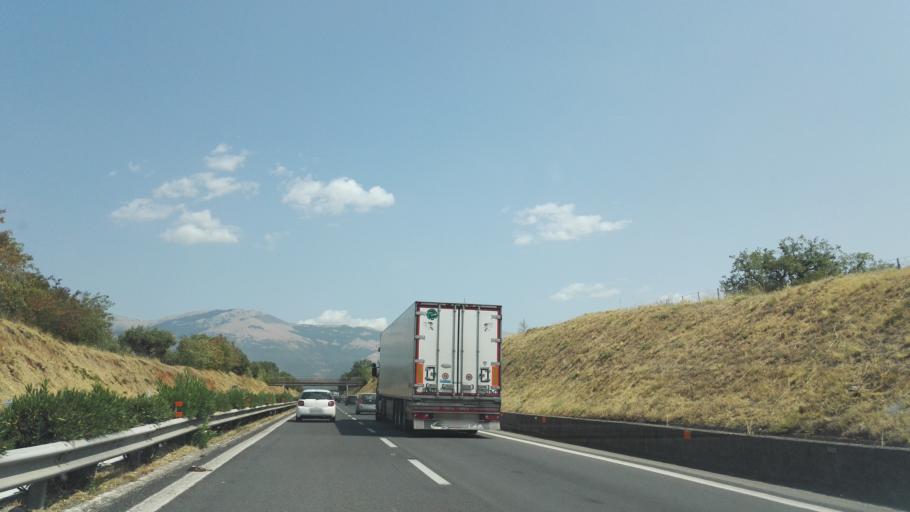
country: IT
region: Calabria
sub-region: Provincia di Cosenza
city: Castrovillari
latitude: 39.7842
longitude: 16.2253
